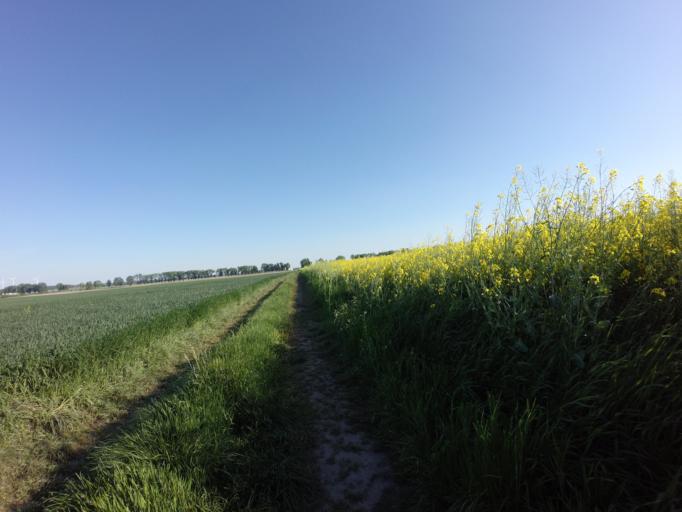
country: PL
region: West Pomeranian Voivodeship
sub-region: Powiat choszczenski
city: Choszczno
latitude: 53.1345
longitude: 15.3887
